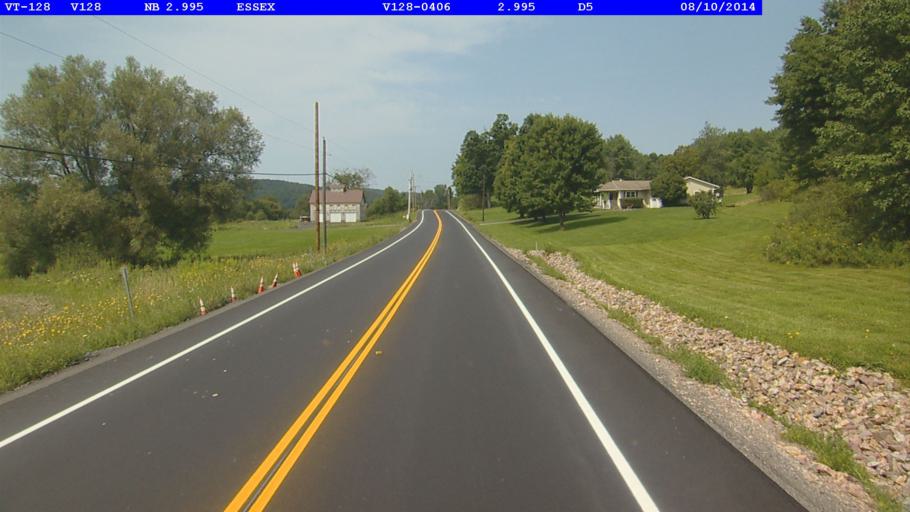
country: US
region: Vermont
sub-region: Chittenden County
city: Jericho
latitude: 44.5409
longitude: -73.0324
